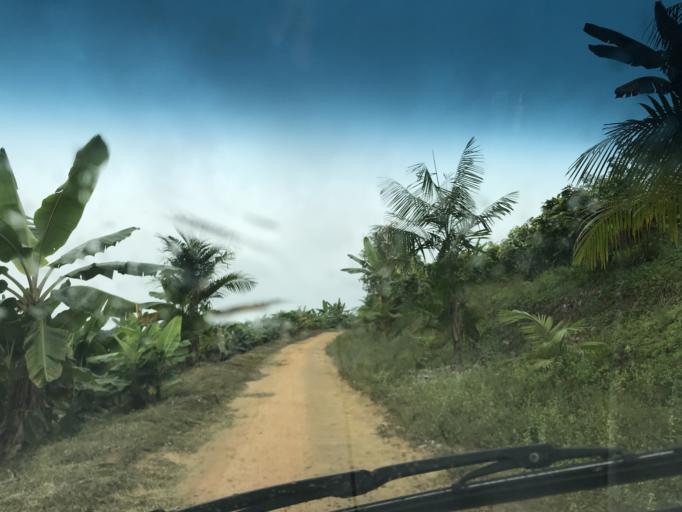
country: BR
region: Bahia
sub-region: Ibirapitanga
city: Ibirapitanga
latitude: -14.0475
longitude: -39.3596
